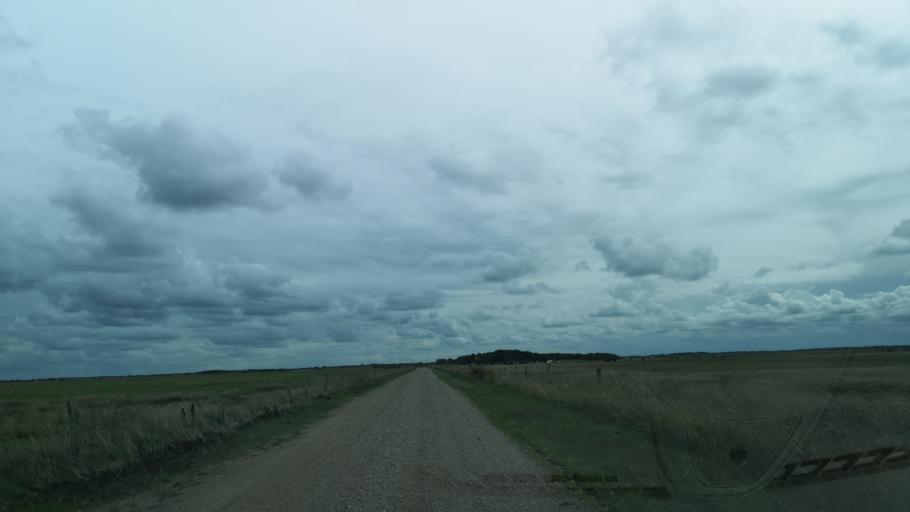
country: DK
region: Central Jutland
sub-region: Ringkobing-Skjern Kommune
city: Hvide Sande
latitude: 55.8647
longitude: 8.2343
